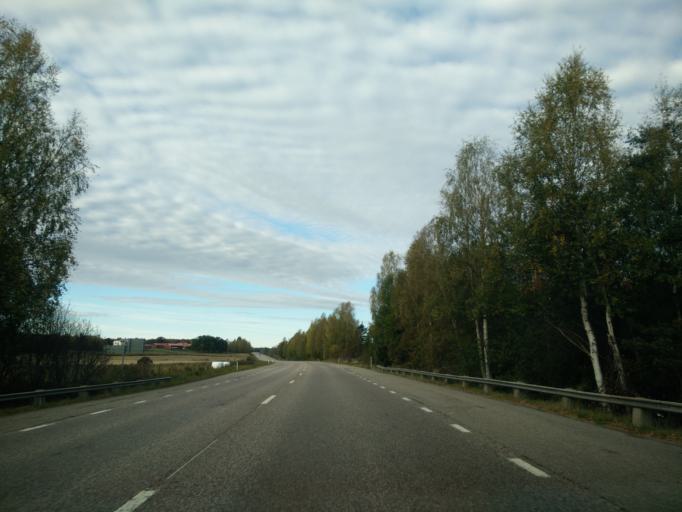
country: SE
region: Gaevleborg
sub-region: Soderhamns Kommun
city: Soderhamn
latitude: 61.2889
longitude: 16.9381
